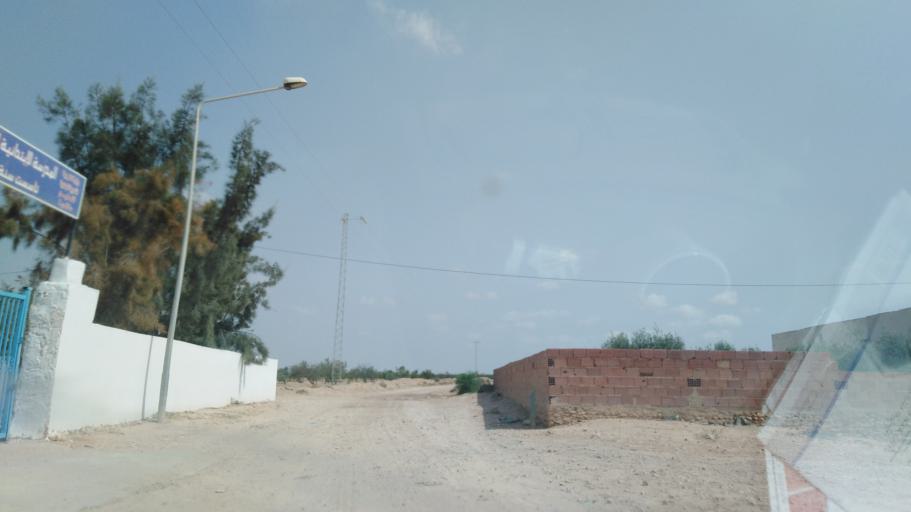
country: TN
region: Safaqis
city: Sfax
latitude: 34.6409
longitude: 10.6173
